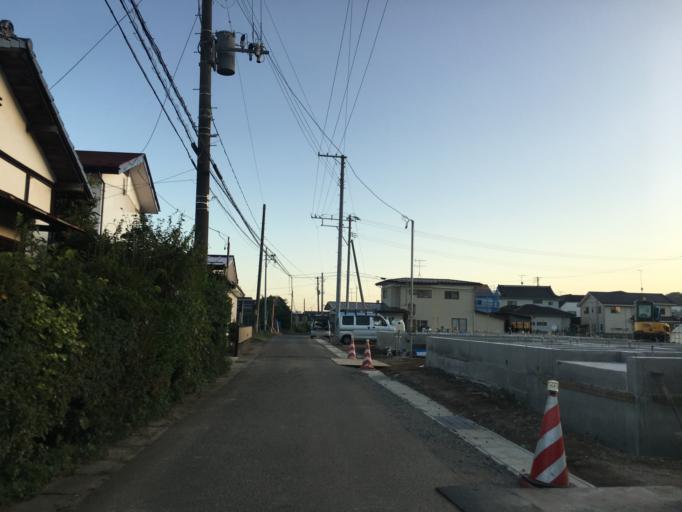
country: JP
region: Fukushima
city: Nihommatsu
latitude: 37.6579
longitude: 140.4804
